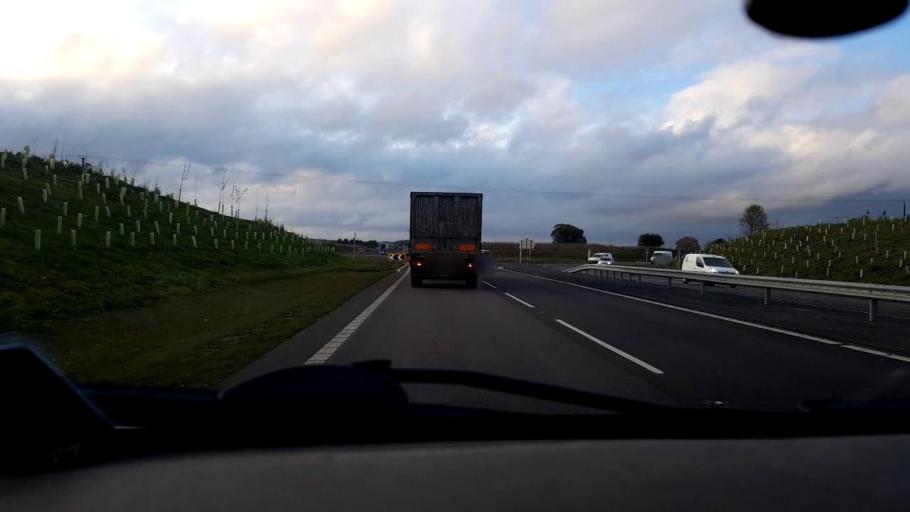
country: GB
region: England
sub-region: Norfolk
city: Horsford
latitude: 52.6860
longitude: 1.2430
